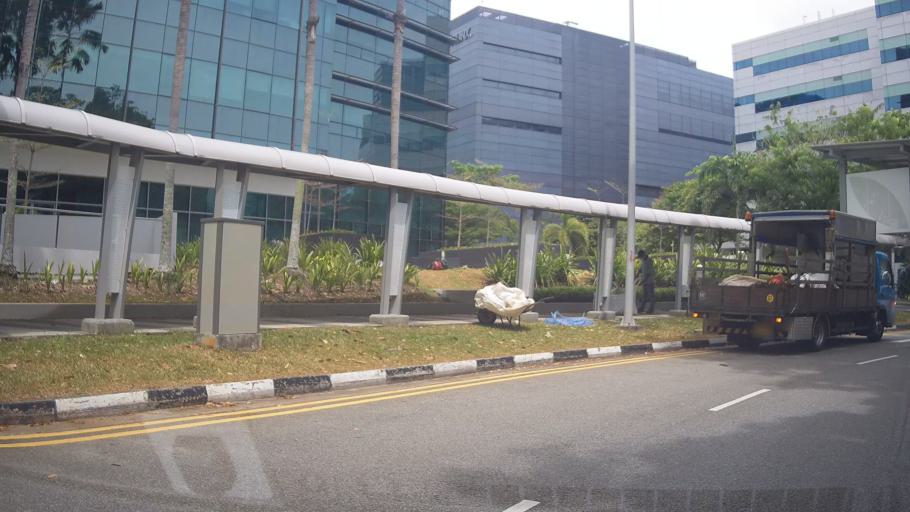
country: SG
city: Singapore
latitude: 1.3375
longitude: 103.9647
